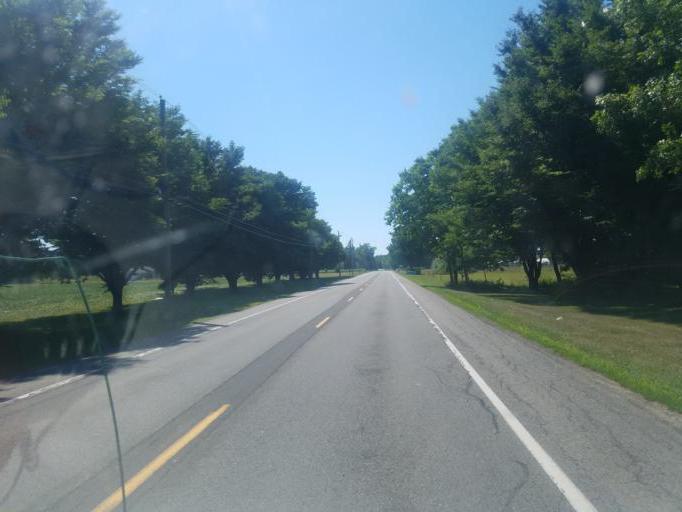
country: US
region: New York
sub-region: Ontario County
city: Phelps
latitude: 42.9490
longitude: -77.0215
